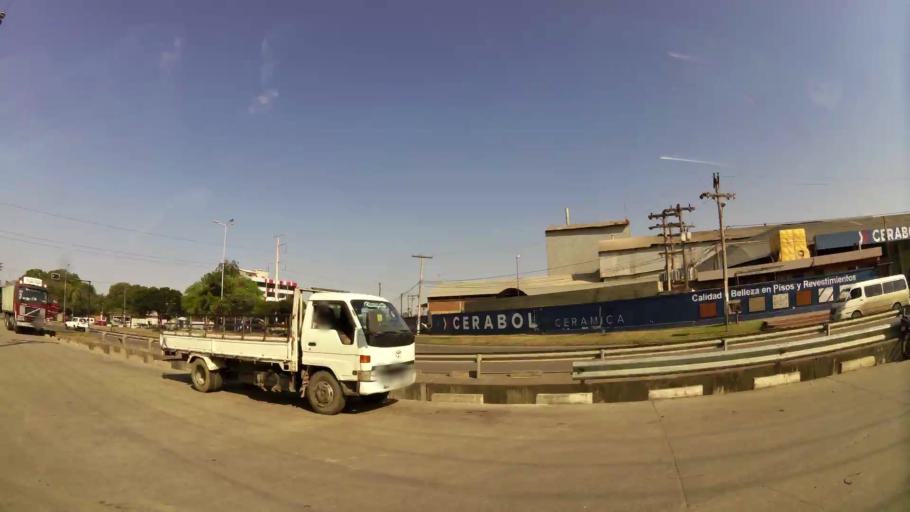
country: BO
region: Santa Cruz
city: Santa Cruz de la Sierra
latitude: -17.7857
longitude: -63.1491
